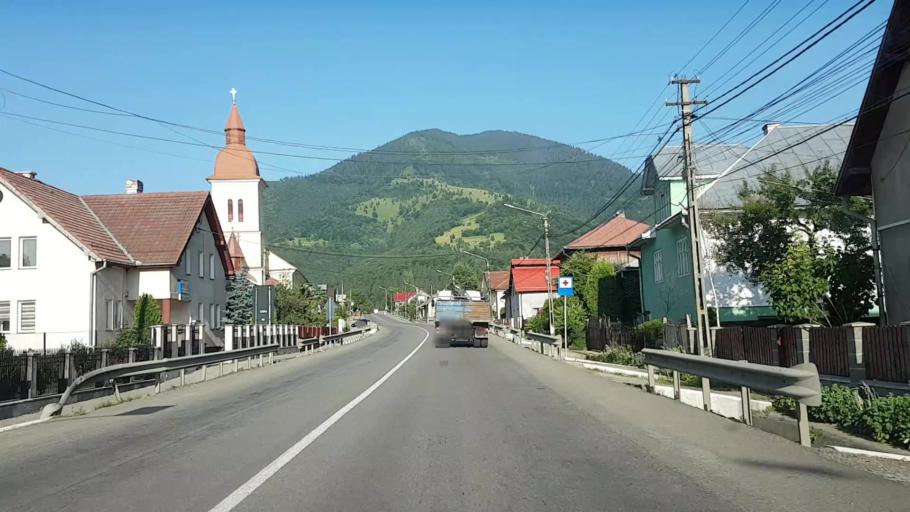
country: RO
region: Bistrita-Nasaud
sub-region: Comuna Tiha Bargaului
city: Tureac
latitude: 47.2103
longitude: 24.8586
